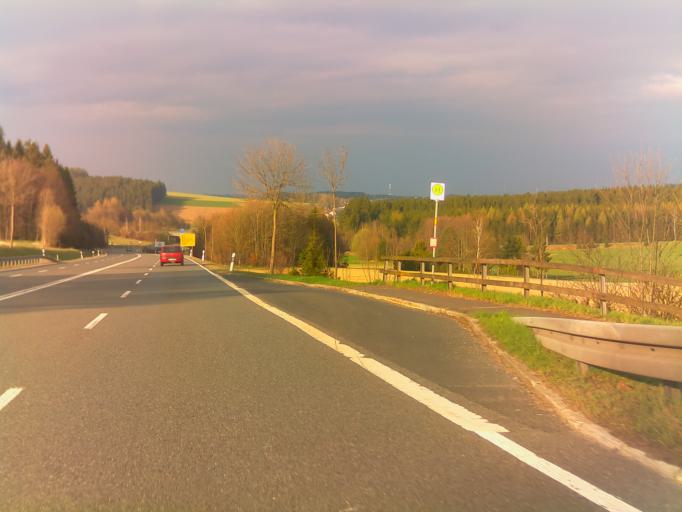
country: DE
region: Bavaria
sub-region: Upper Franconia
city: Leupoldsgrun
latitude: 50.2966
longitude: 11.8210
